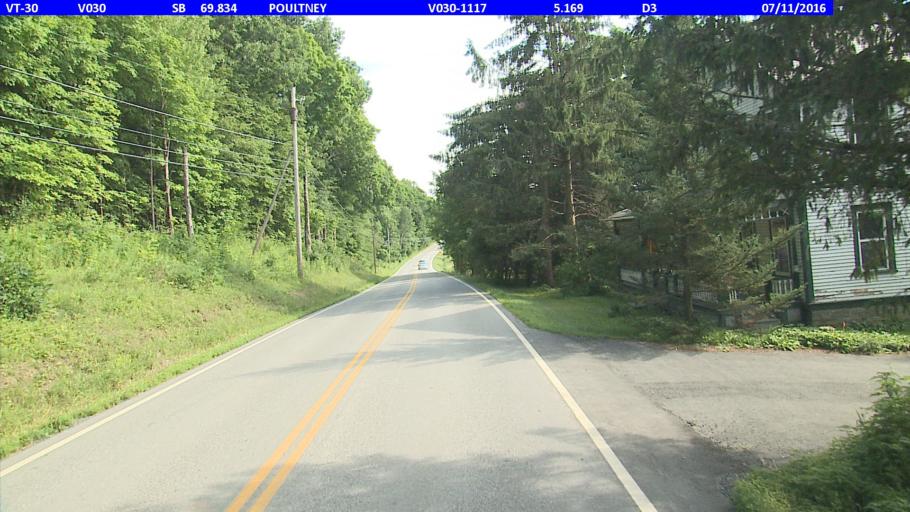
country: US
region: Vermont
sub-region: Rutland County
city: Poultney
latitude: 43.5257
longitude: -73.2316
